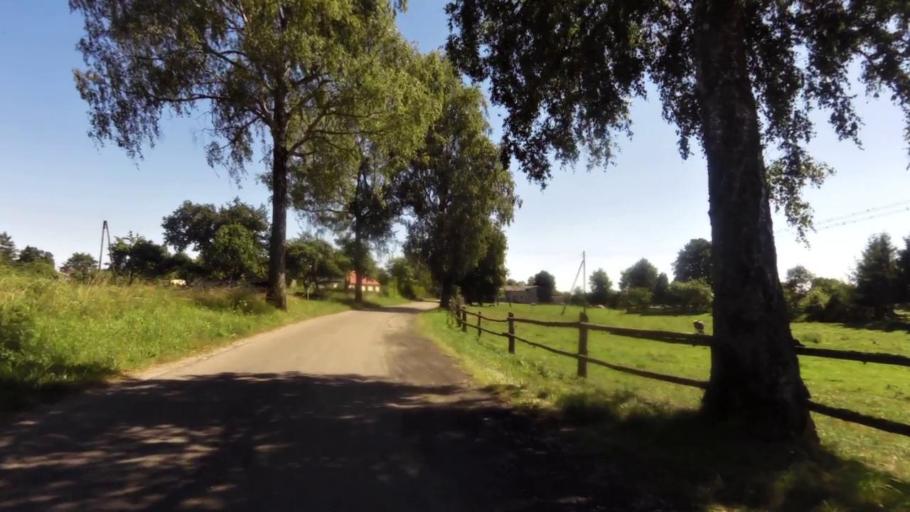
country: PL
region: West Pomeranian Voivodeship
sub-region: Powiat szczecinecki
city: Bialy Bor
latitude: 53.8941
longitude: 16.8821
